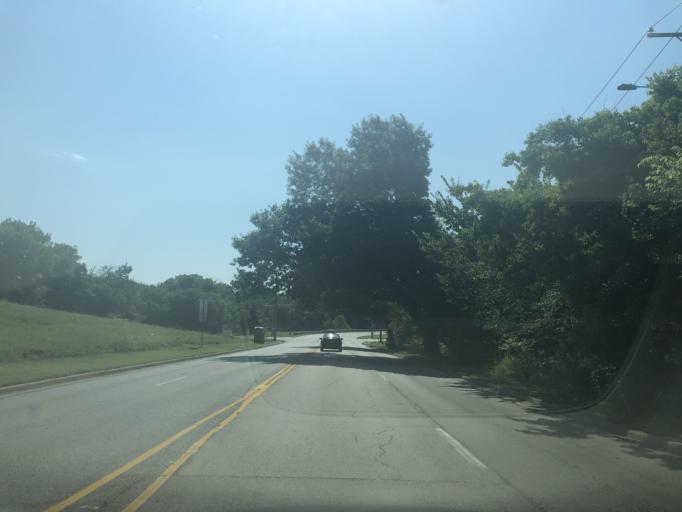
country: US
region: Texas
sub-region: Dallas County
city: Grand Prairie
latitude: 32.7211
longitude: -97.0209
